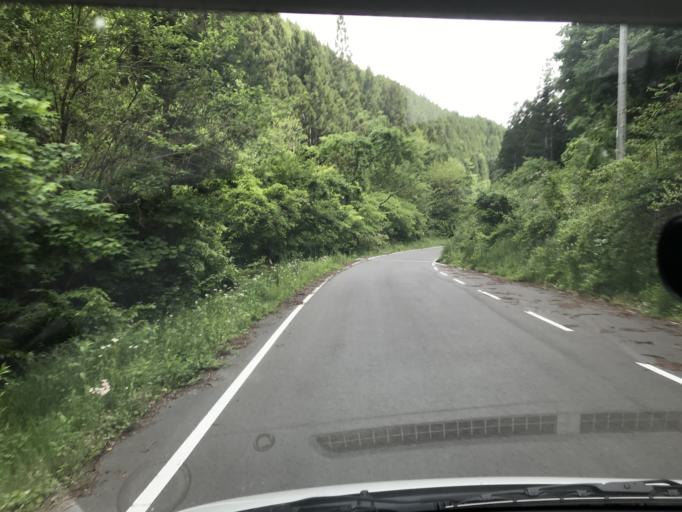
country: JP
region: Miyagi
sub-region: Oshika Gun
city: Onagawa Cho
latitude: 38.6793
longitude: 141.3473
